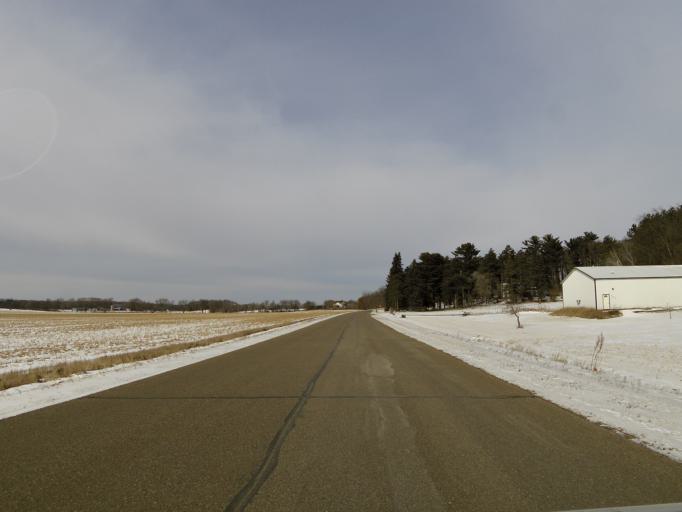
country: US
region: Minnesota
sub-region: Washington County
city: Stillwater
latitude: 45.0630
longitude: -92.7753
